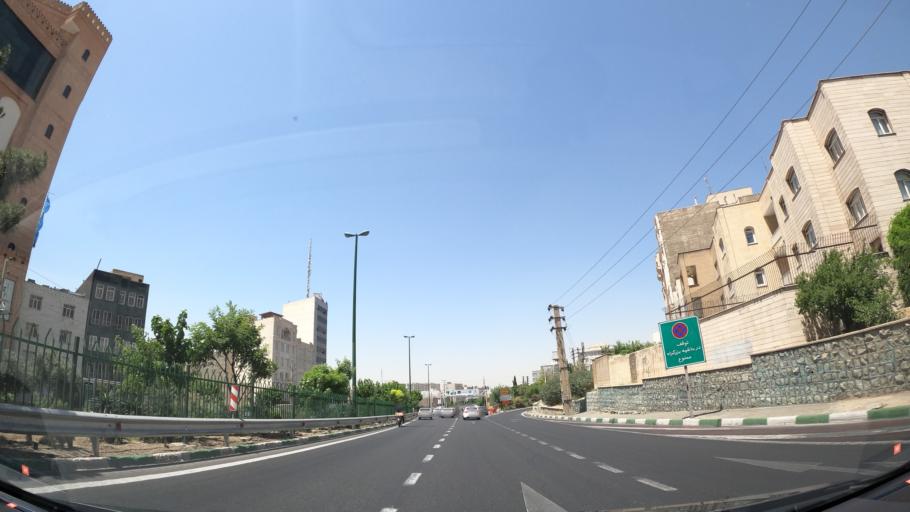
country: IR
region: Tehran
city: Tajrish
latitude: 35.7650
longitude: 51.3054
